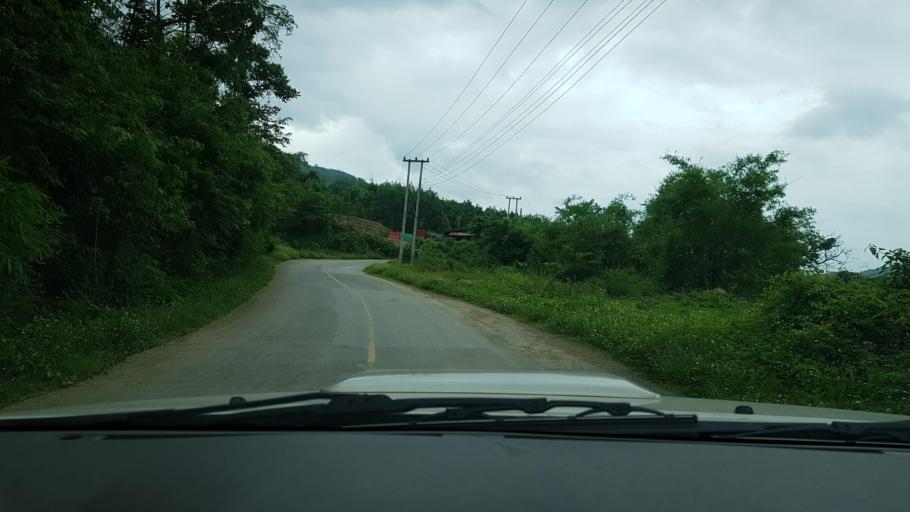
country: LA
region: Loungnamtha
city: Muang Nale
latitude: 20.2299
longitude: 101.5629
